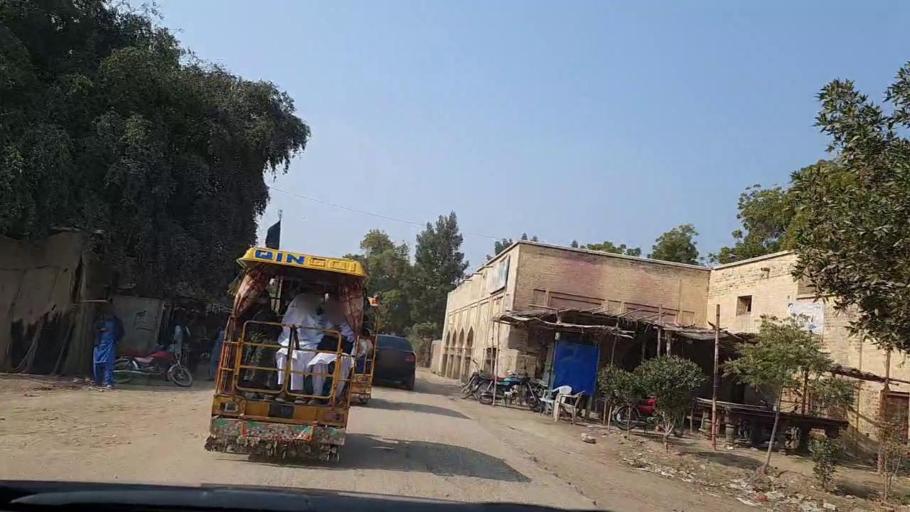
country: PK
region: Sindh
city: Sakrand
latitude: 26.1420
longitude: 68.2736
